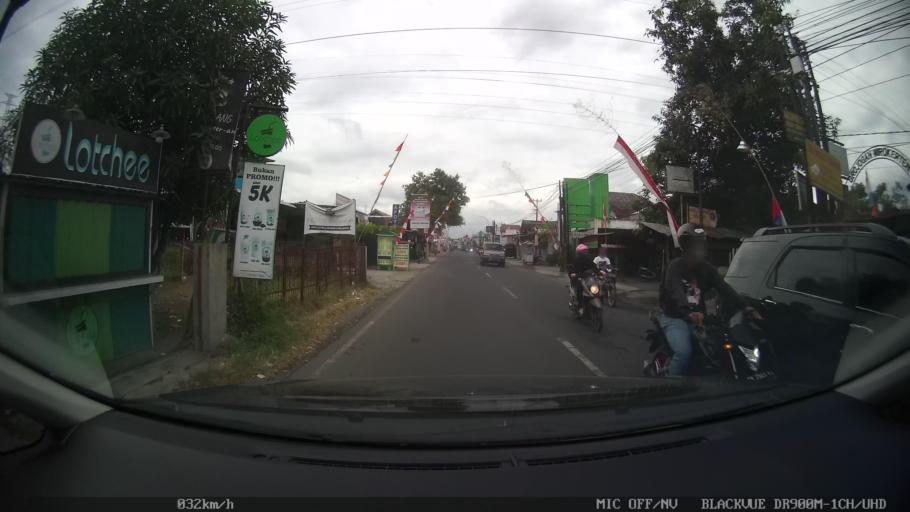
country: ID
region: Daerah Istimewa Yogyakarta
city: Sewon
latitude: -7.8472
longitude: 110.3908
